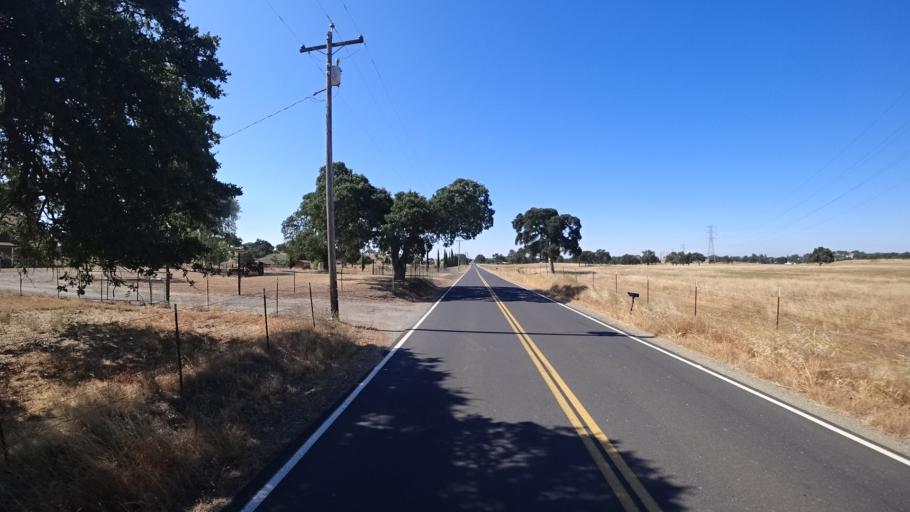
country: US
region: California
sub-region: Calaveras County
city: Rancho Calaveras
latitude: 38.1024
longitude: -120.9086
